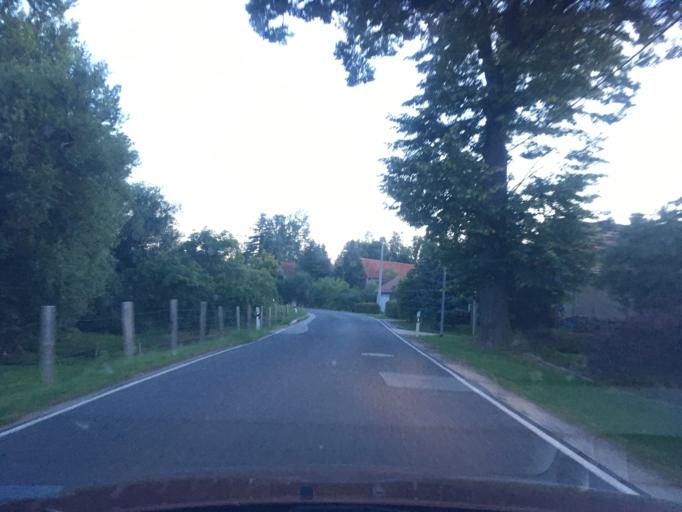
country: PL
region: Lower Silesian Voivodeship
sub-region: Powiat zgorzelecki
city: Piensk
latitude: 51.2162
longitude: 15.0028
